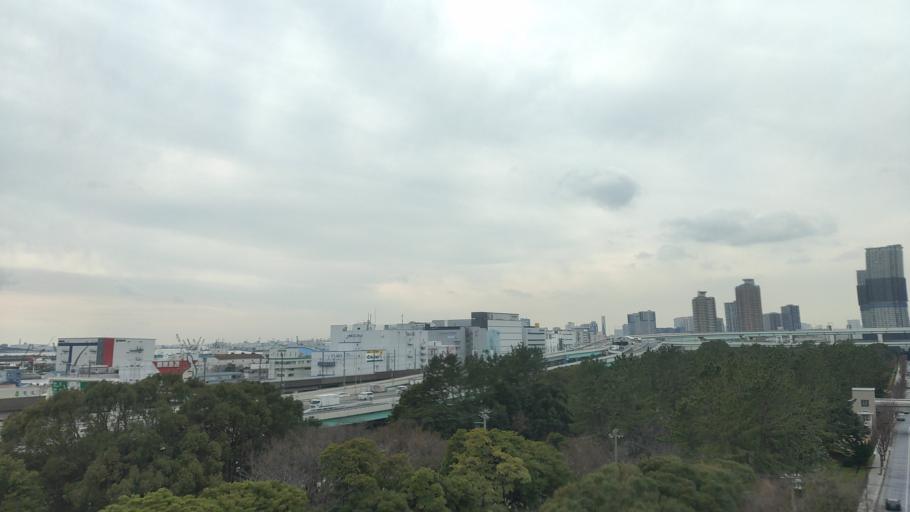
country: JP
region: Tokyo
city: Urayasu
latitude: 35.6472
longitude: 139.8208
